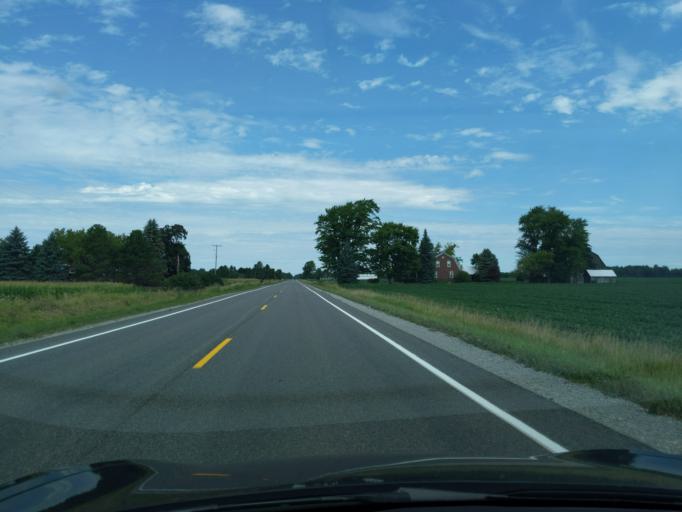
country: US
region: Michigan
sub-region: Gratiot County
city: Breckenridge
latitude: 43.4989
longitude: -84.3698
